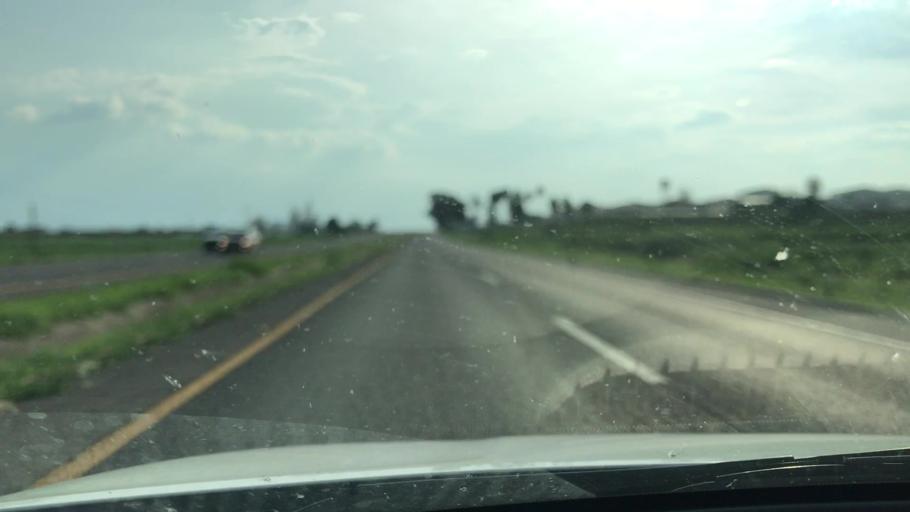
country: MX
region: Guanajuato
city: Penjamo
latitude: 20.3814
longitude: -101.8161
